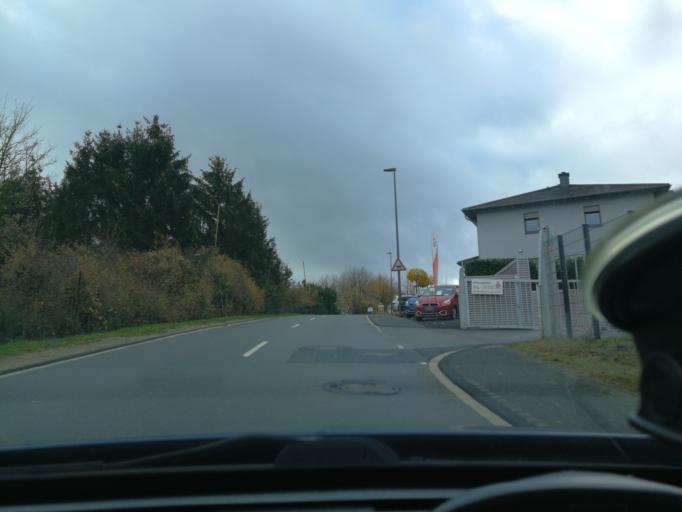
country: DE
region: Rheinland-Pfalz
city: Aach
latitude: 49.7719
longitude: 6.5926
